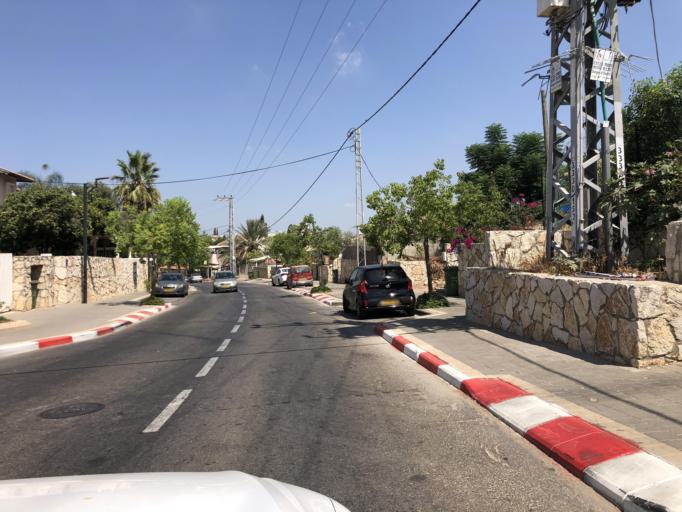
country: IL
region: Central District
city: Rosh Ha'Ayin
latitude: 32.0984
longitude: 34.9568
